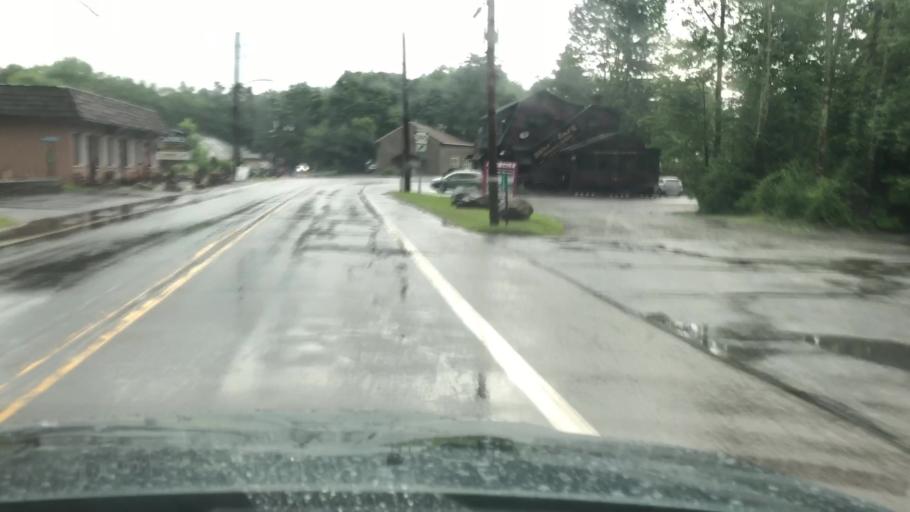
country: US
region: Pennsylvania
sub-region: Monroe County
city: Mountainhome
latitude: 41.1798
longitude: -75.2691
